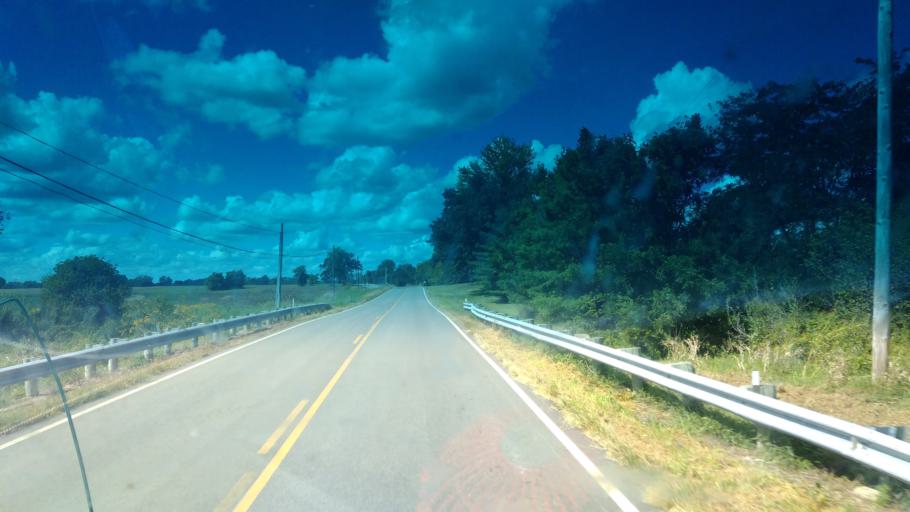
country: US
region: Ohio
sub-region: Champaign County
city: North Lewisburg
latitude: 40.1980
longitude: -83.4788
